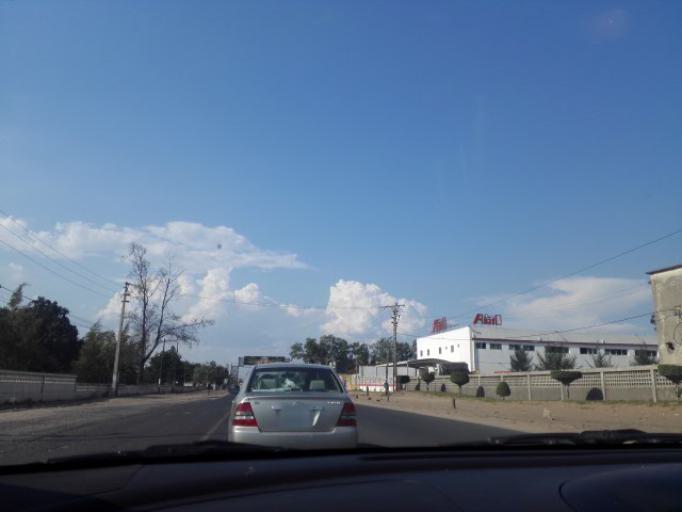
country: MZ
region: Maputo City
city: Maputo
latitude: -25.8612
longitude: 32.5666
